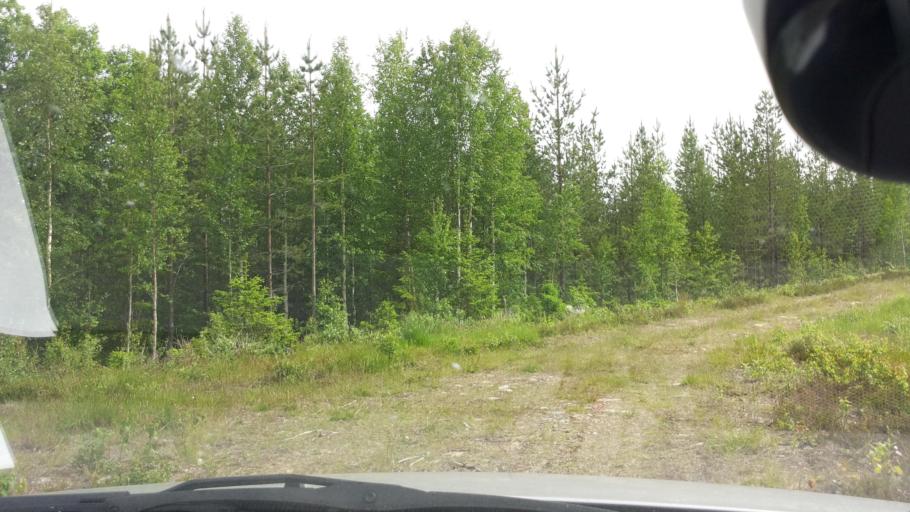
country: SE
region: Gaevleborg
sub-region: Ovanakers Kommun
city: Edsbyn
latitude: 61.4542
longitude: 15.3241
